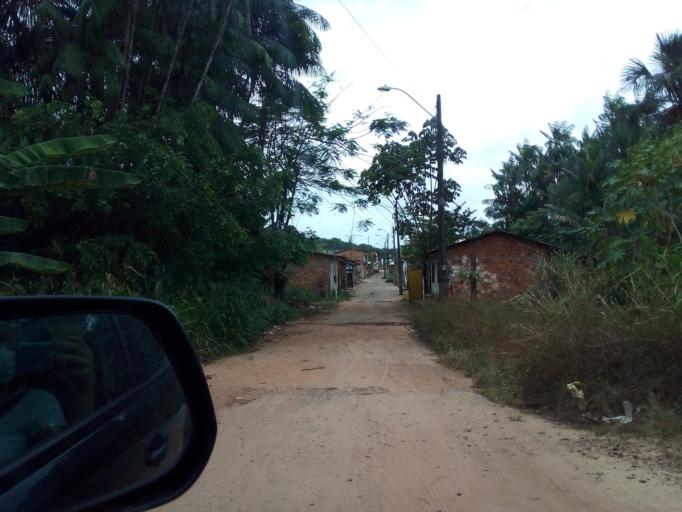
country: BR
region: Maranhao
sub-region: Sao Luis
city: Sao Luis
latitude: -2.6755
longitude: -44.2960
